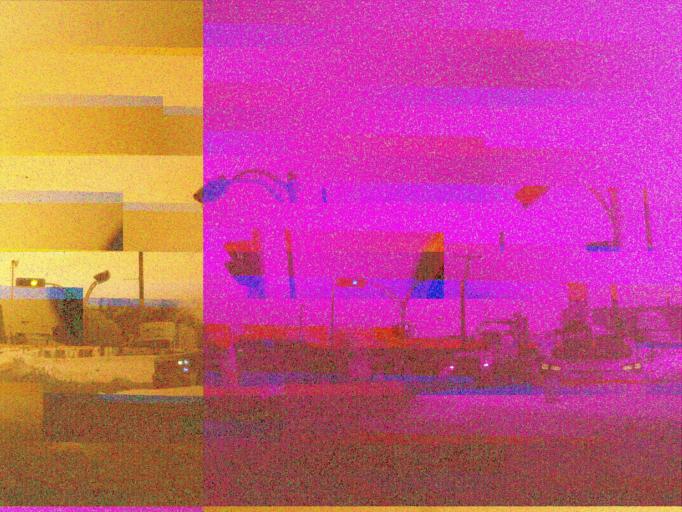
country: CA
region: Quebec
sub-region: Montreal
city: Saint-Leonard
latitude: 45.6162
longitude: -73.5610
